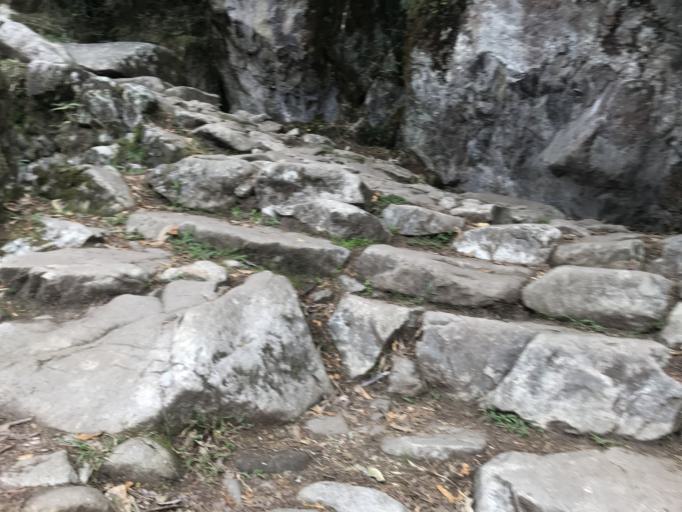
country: PE
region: Cusco
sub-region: Provincia de La Convencion
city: Santa Teresa
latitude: -13.1681
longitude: -72.5429
